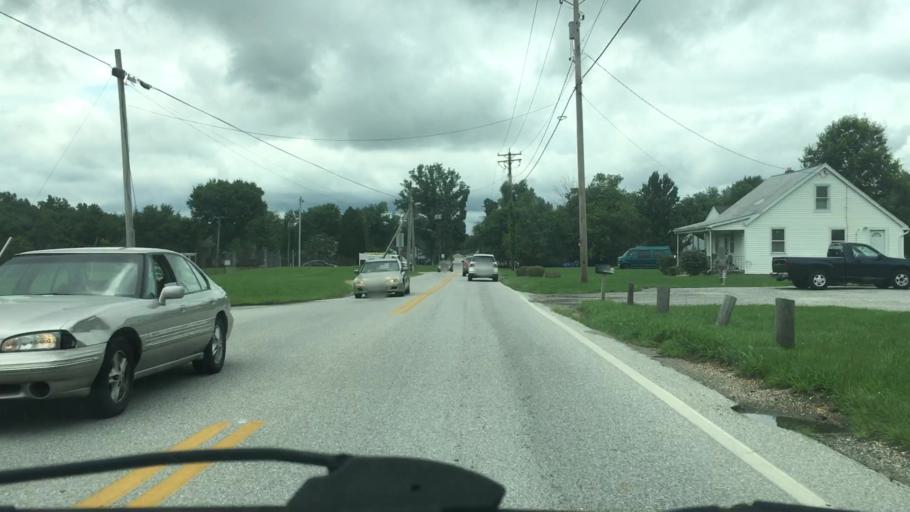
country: US
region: Maryland
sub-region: Howard County
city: Savage
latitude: 39.1688
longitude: -76.8307
